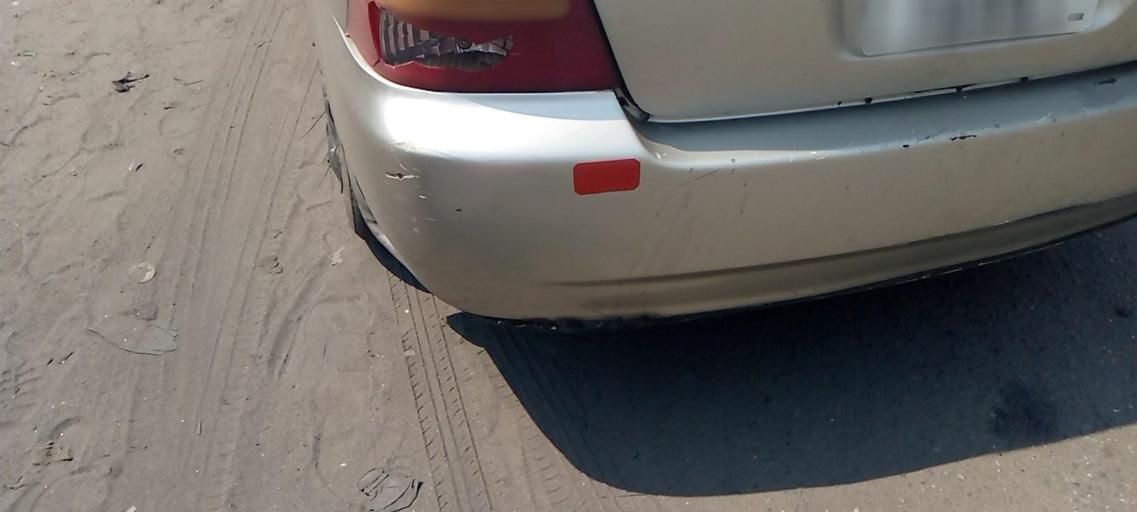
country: ZM
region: Lusaka
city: Lusaka
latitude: -15.4015
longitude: 28.3560
